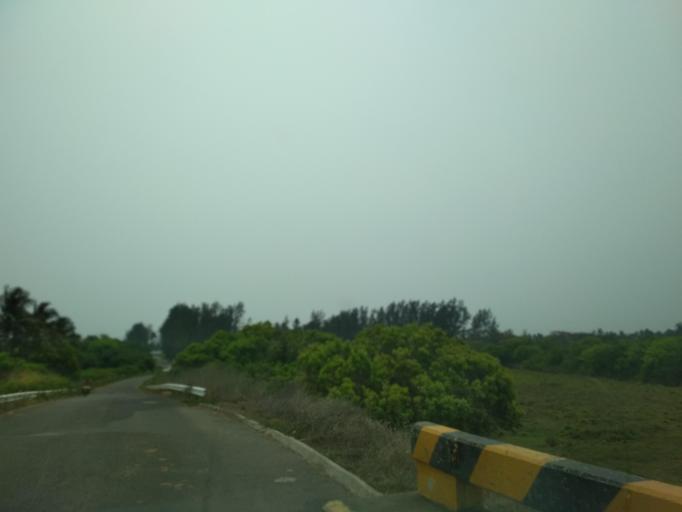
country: MX
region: Veracruz
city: Anton Lizardo
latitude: 19.0395
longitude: -95.9741
